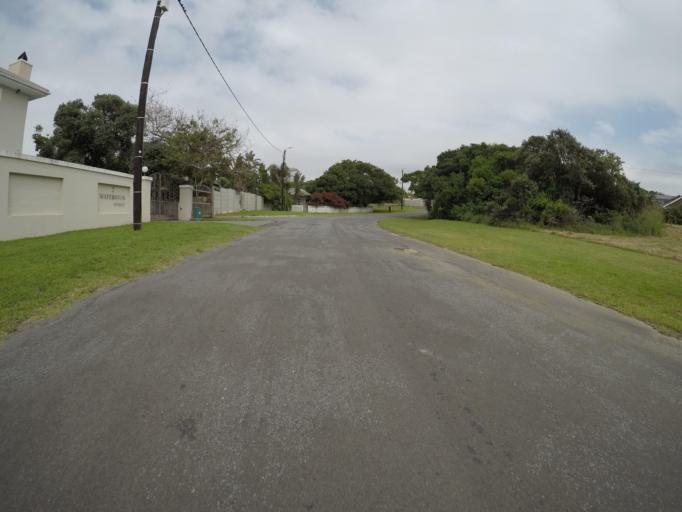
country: ZA
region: Eastern Cape
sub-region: Buffalo City Metropolitan Municipality
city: East London
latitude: -32.9383
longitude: 28.0267
